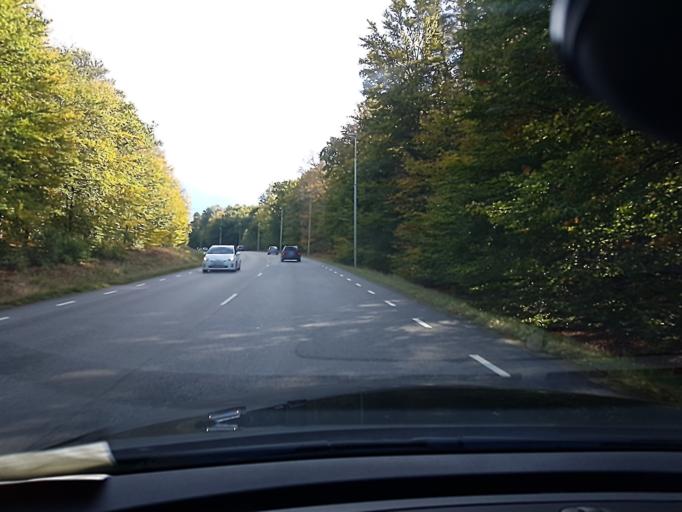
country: SE
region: Kronoberg
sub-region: Vaxjo Kommun
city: Vaexjoe
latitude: 56.8665
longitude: 14.7898
